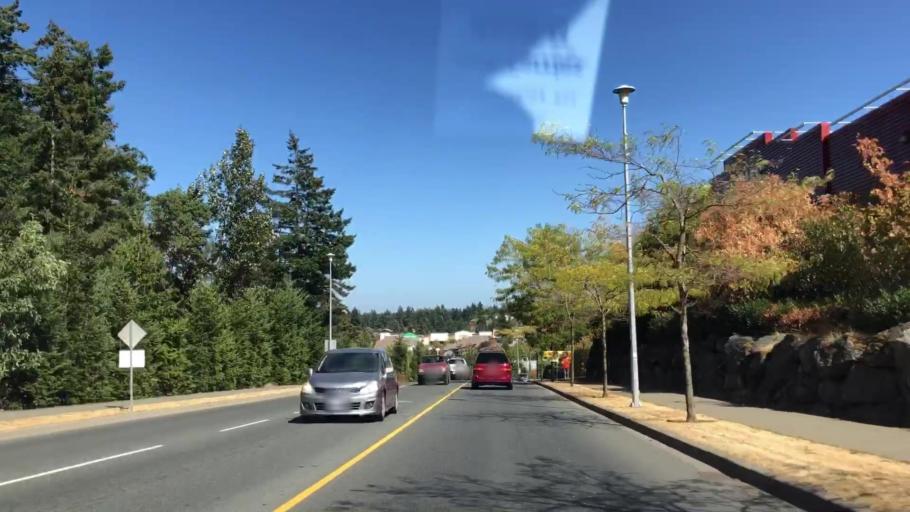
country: CA
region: British Columbia
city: Langford
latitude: 48.4595
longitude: -123.5014
